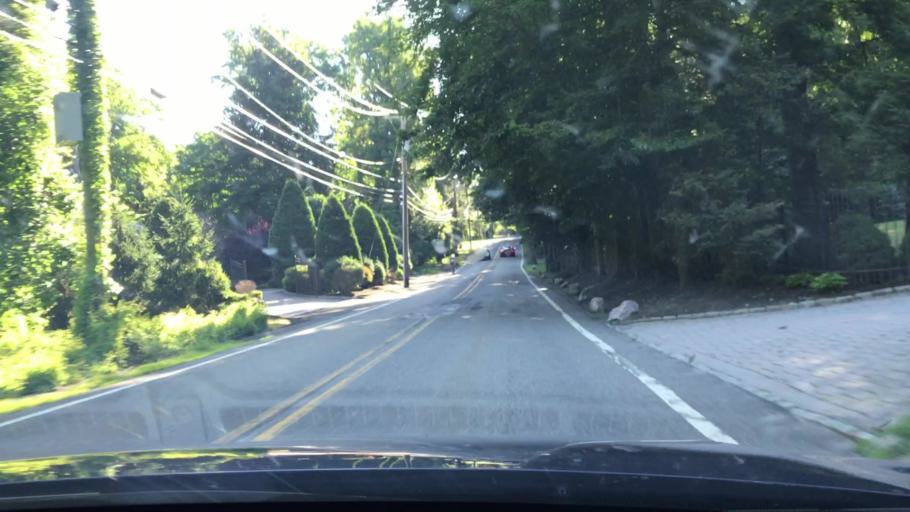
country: US
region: New Jersey
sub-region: Bergen County
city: Alpine
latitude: 40.9429
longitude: -73.9367
